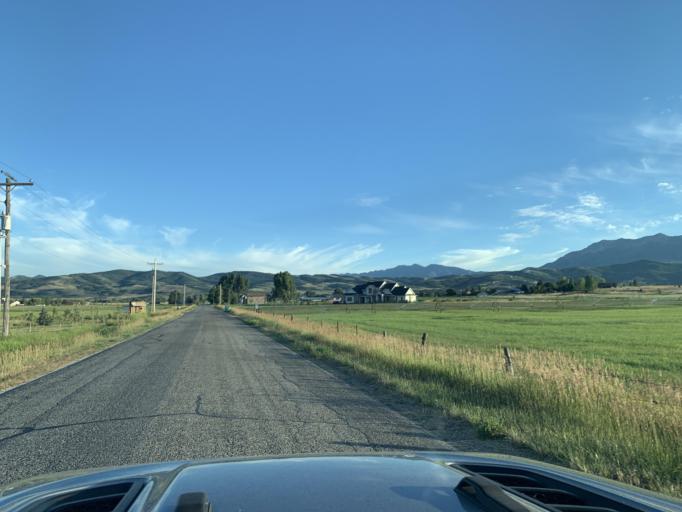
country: US
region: Utah
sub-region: Weber County
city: Wolf Creek
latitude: 41.2743
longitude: -111.7619
